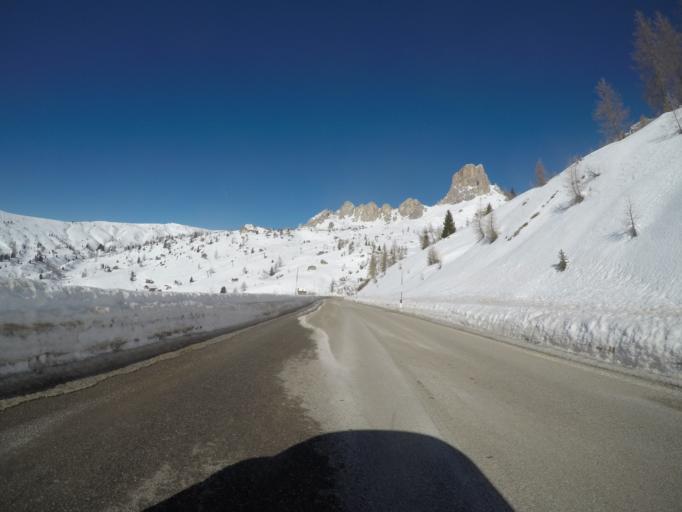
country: IT
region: Veneto
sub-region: Provincia di Belluno
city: Selva di Cadore
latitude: 46.4863
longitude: 12.0390
